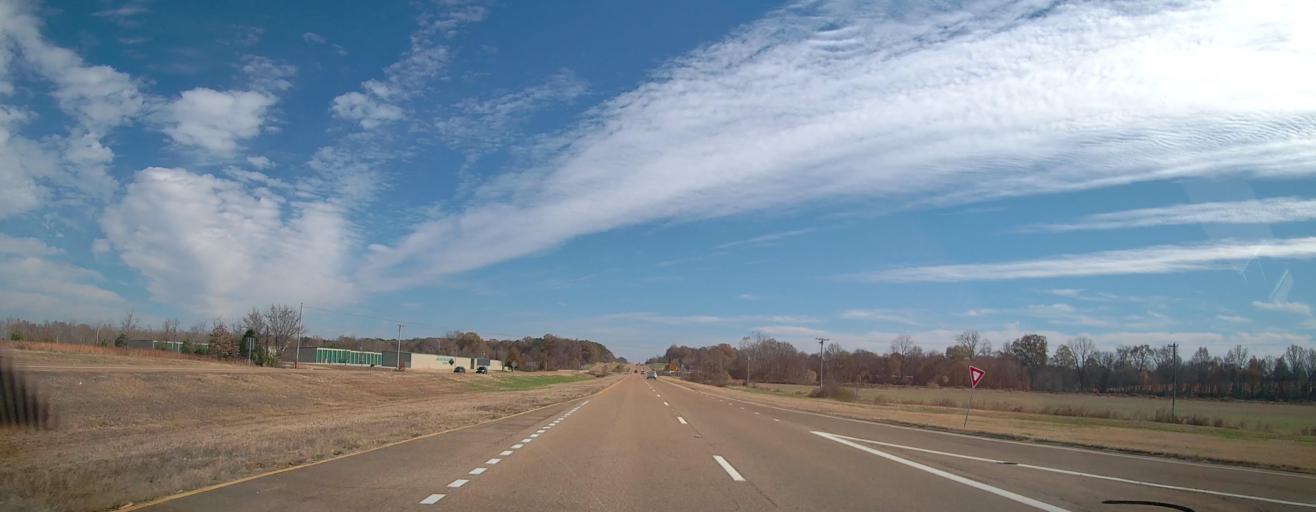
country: US
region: Mississippi
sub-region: Benton County
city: Ashland
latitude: 34.9462
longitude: -89.2971
